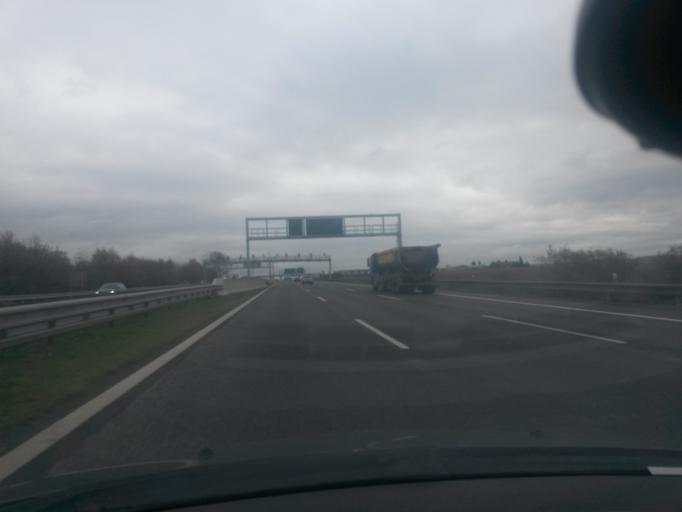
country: CZ
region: Central Bohemia
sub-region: Okres Praha-Zapad
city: Pruhonice
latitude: 49.9979
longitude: 14.5794
